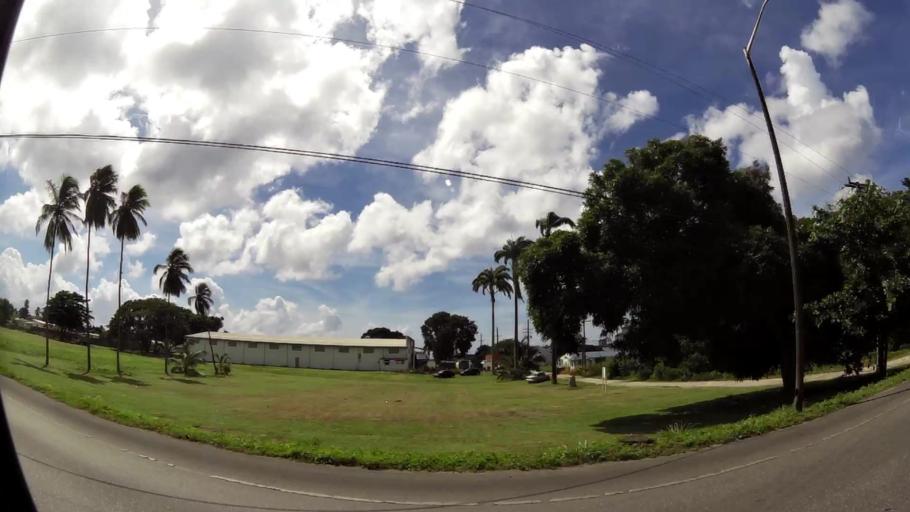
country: BB
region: Saint Michael
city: Bridgetown
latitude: 13.1240
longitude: -59.6289
